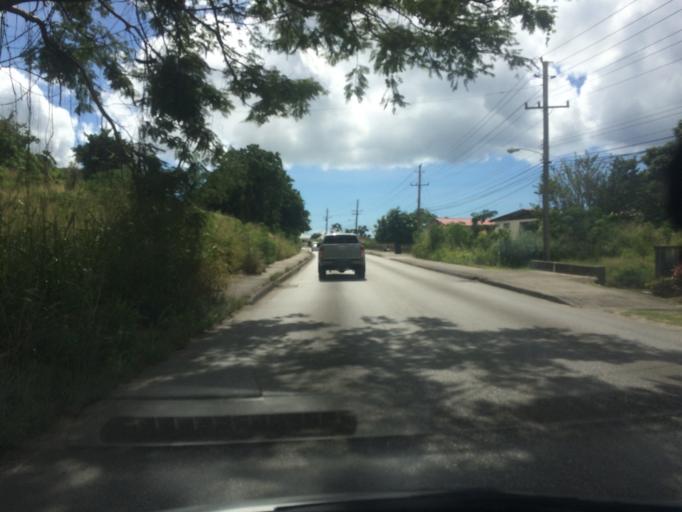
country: BB
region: Saint James
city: Holetown
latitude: 13.1668
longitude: -59.6136
